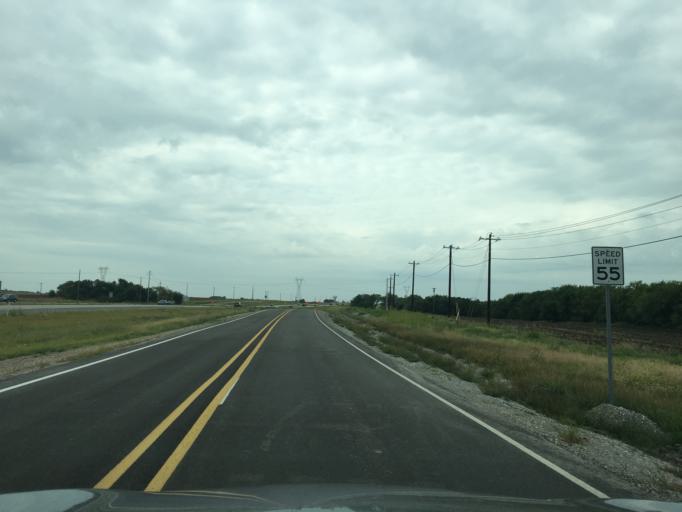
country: US
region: Texas
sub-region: Grayson County
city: Van Alstyne
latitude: 33.3801
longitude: -96.5814
